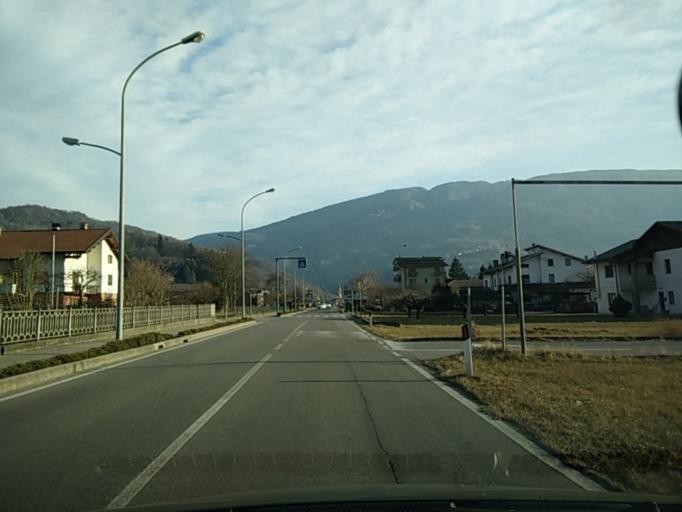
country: IT
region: Veneto
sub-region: Provincia di Belluno
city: Farra d'Alpago
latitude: 46.1284
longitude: 12.3492
